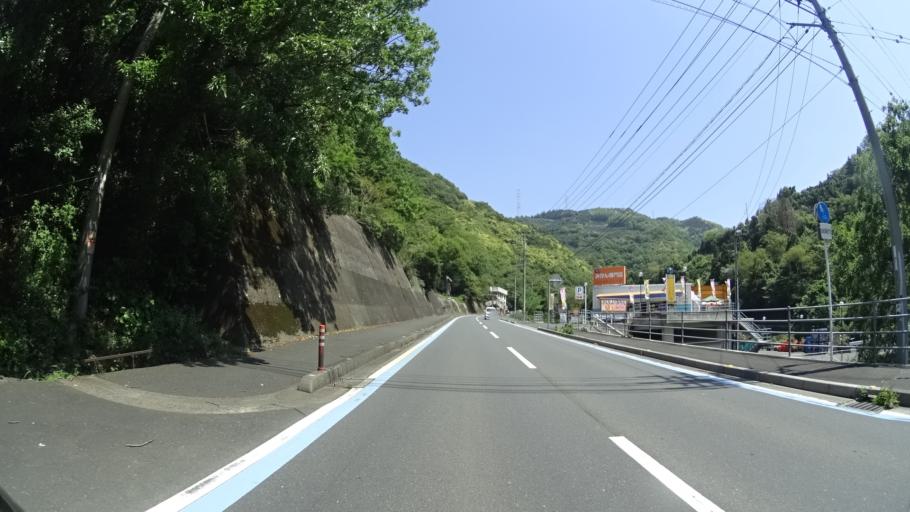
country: JP
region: Ehime
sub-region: Nishiuwa-gun
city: Ikata-cho
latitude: 33.4954
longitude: 132.3674
